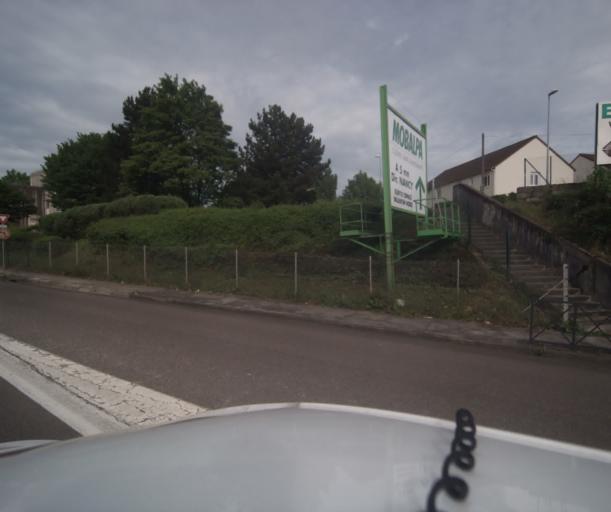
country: FR
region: Franche-Comte
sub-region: Departement du Doubs
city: Avanne-Aveney
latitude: 47.2287
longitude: 5.9804
